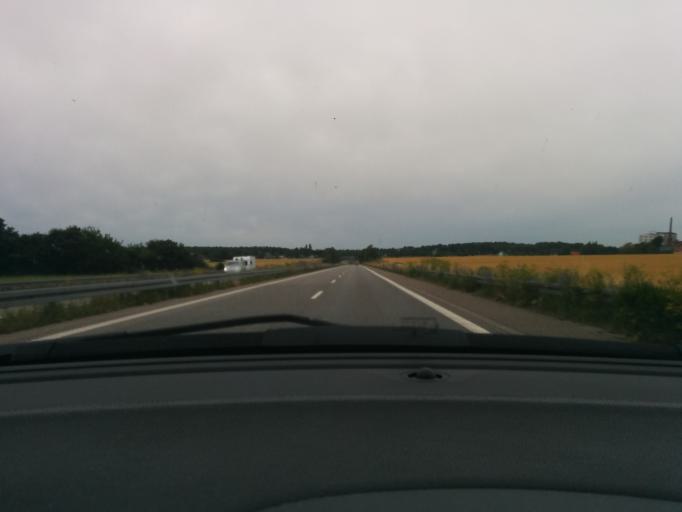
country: DK
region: Zealand
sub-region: Guldborgsund Kommune
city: Sakskobing
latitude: 54.7993
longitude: 11.6695
